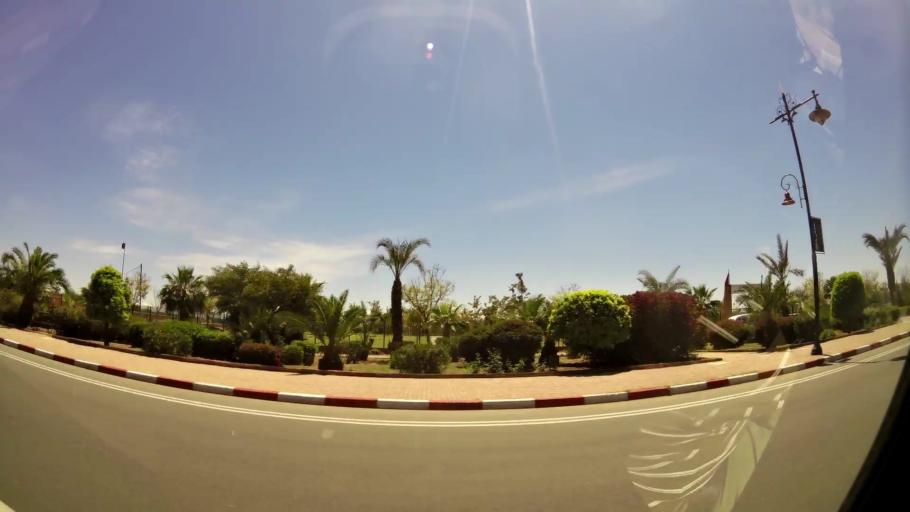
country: MA
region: Marrakech-Tensift-Al Haouz
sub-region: Marrakech
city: Marrakesh
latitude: 31.6190
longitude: -8.0056
